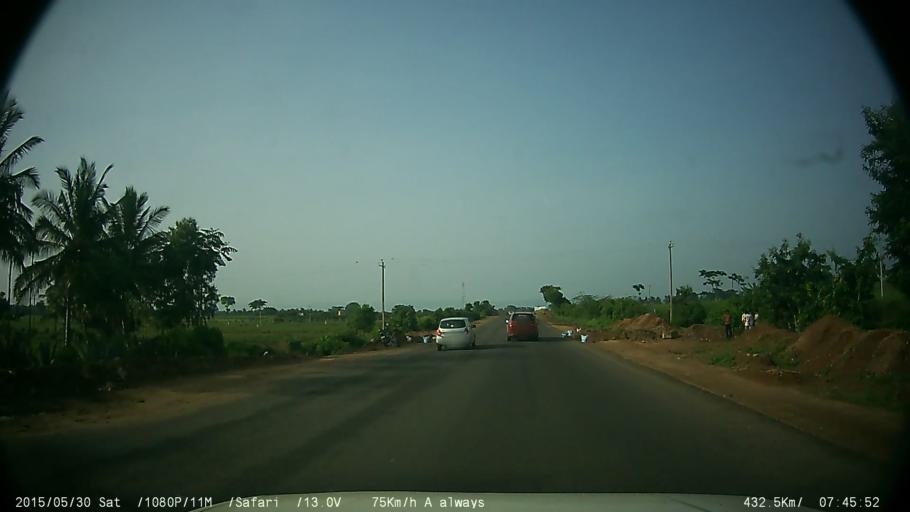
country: IN
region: Karnataka
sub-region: Chamrajnagar
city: Gundlupet
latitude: 11.8903
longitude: 76.6652
